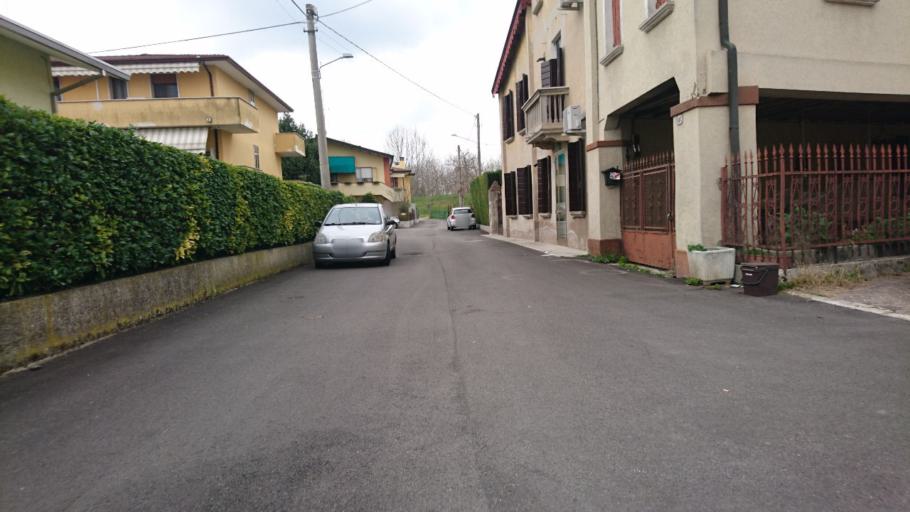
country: IT
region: Veneto
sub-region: Provincia di Padova
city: Vigodarzere
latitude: 45.4521
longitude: 11.8650
